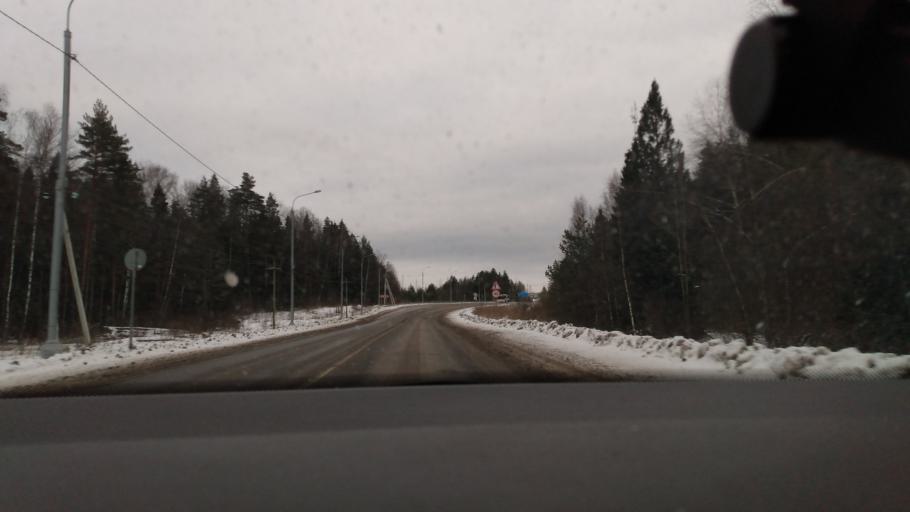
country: RU
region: Moskovskaya
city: Yegor'yevsk
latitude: 55.3108
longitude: 39.0772
